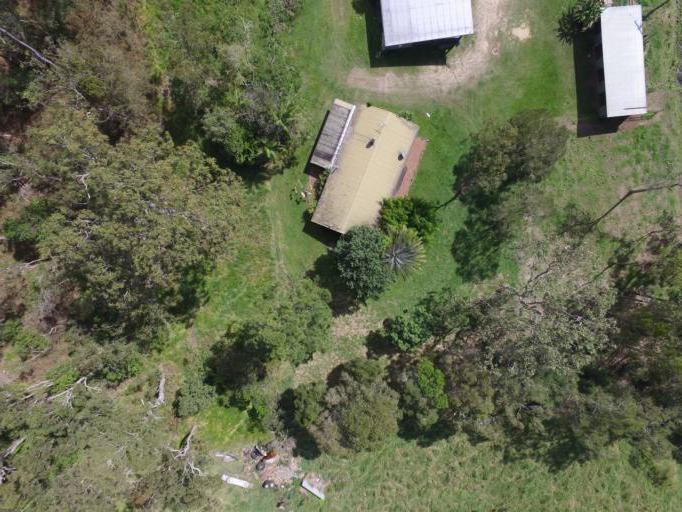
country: AU
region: Queensland
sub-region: Tablelands
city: Atherton
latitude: -17.3035
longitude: 145.4572
